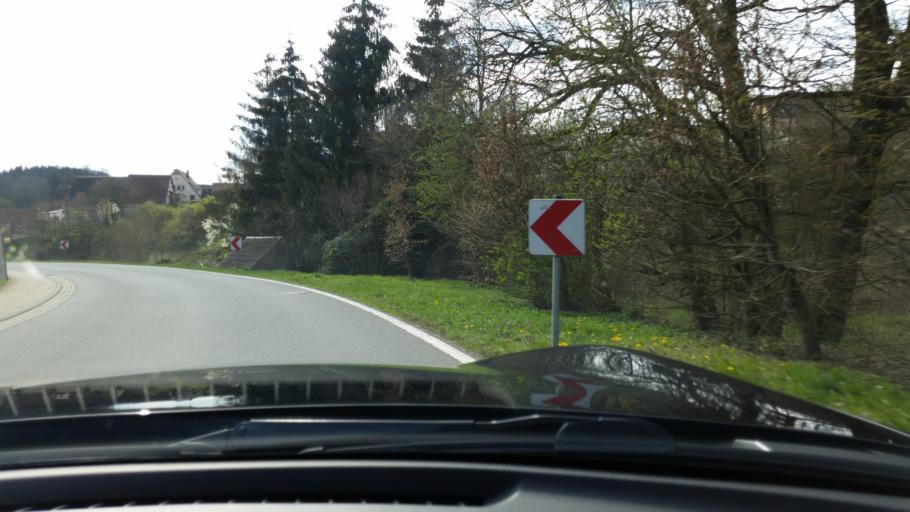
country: DE
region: Baden-Wuerttemberg
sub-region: Regierungsbezirk Stuttgart
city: Forchtenberg
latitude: 49.3725
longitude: 9.5438
